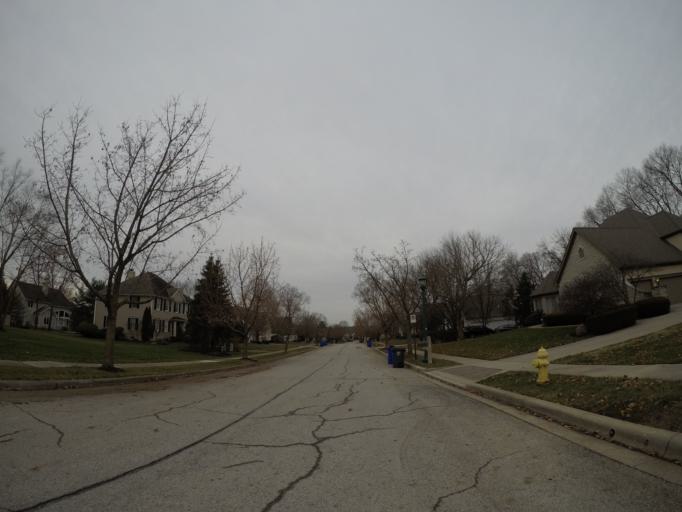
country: US
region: Ohio
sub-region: Franklin County
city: Dublin
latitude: 40.0627
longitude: -83.0965
